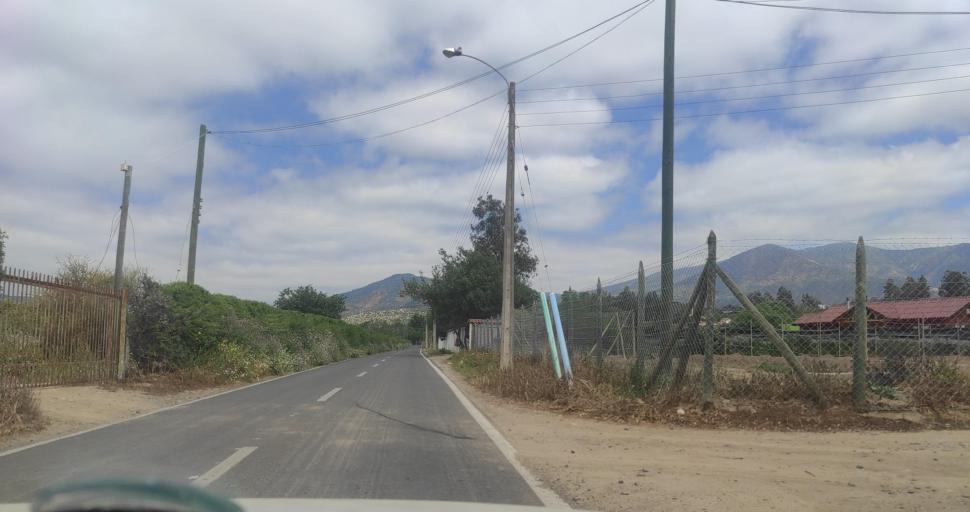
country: CL
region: Valparaiso
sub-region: Provincia de Marga Marga
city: Limache
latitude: -33.0343
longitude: -71.2314
